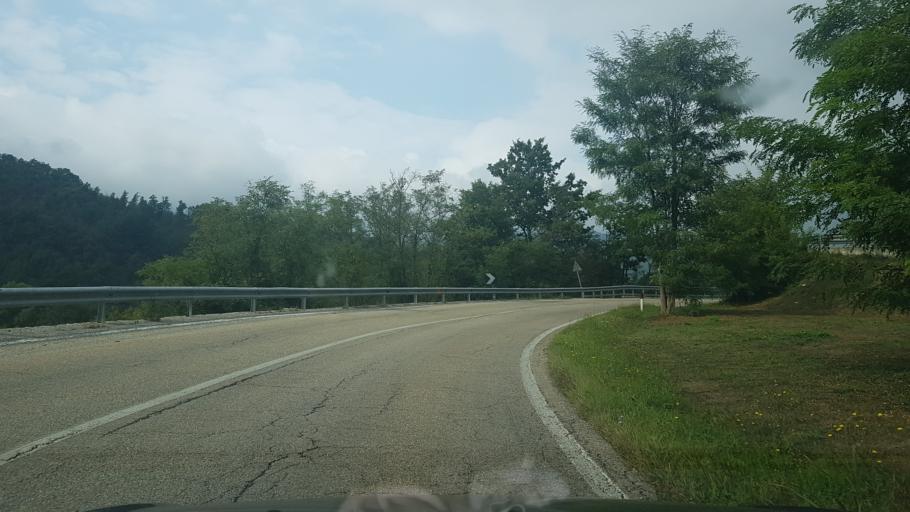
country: IT
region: Piedmont
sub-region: Provincia di Cuneo
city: Monesiglio
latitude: 44.4784
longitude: 8.1133
